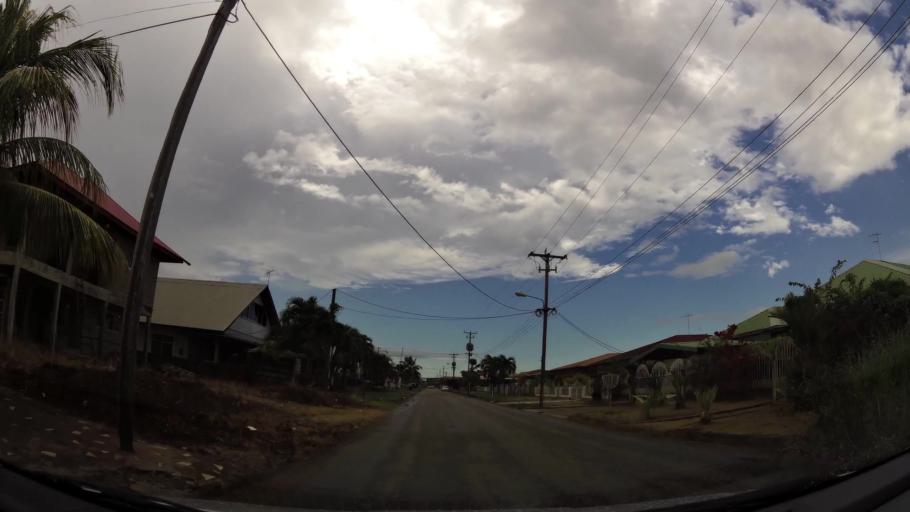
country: SR
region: Commewijne
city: Nieuw Amsterdam
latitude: 5.8610
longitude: -55.1220
